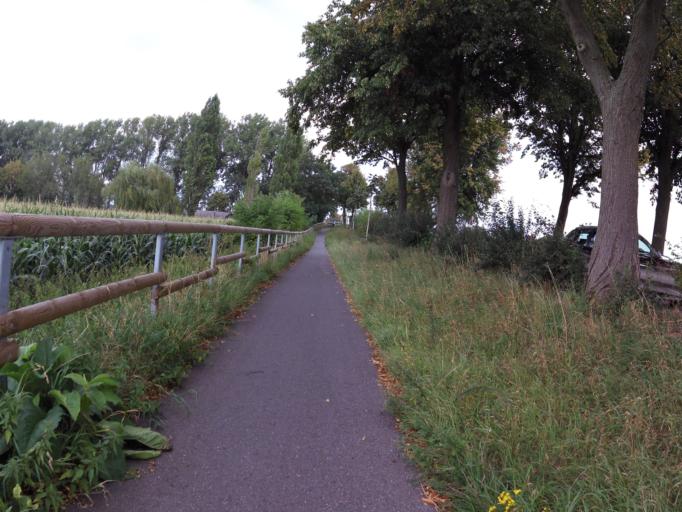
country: DE
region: Lower Saxony
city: Blender
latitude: 52.9245
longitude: 9.1730
